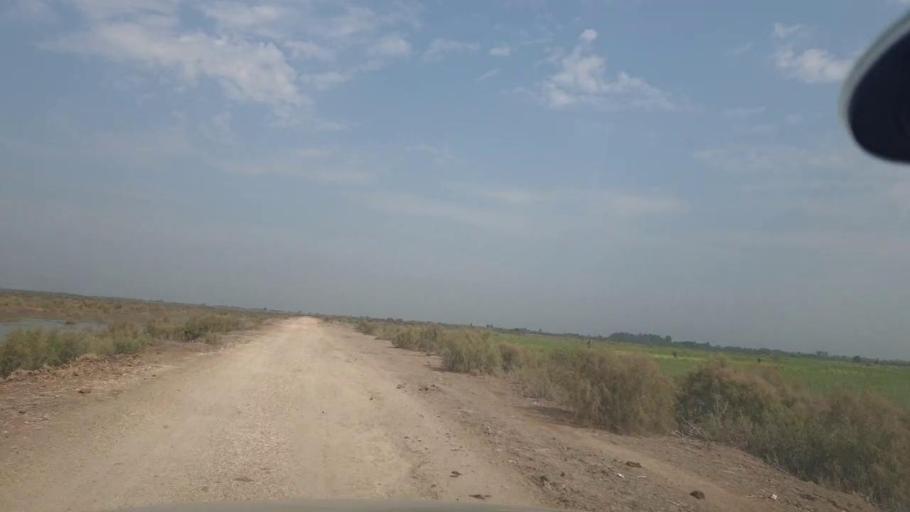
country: PK
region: Balochistan
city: Mehrabpur
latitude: 28.0401
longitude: 68.1243
